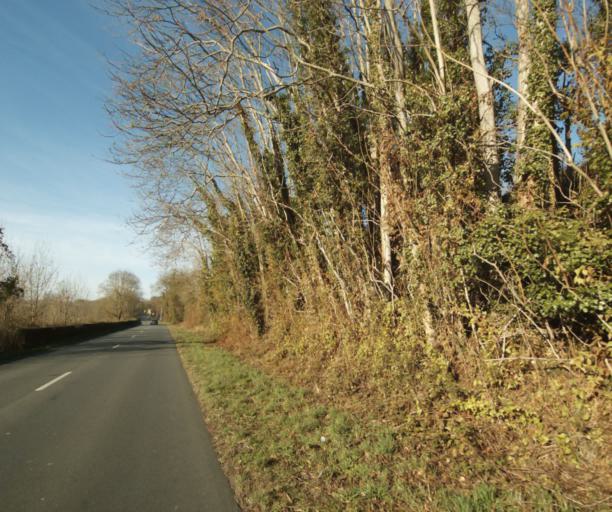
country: FR
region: Poitou-Charentes
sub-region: Departement de la Charente-Maritime
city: Les Gonds
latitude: 45.7310
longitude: -0.6001
